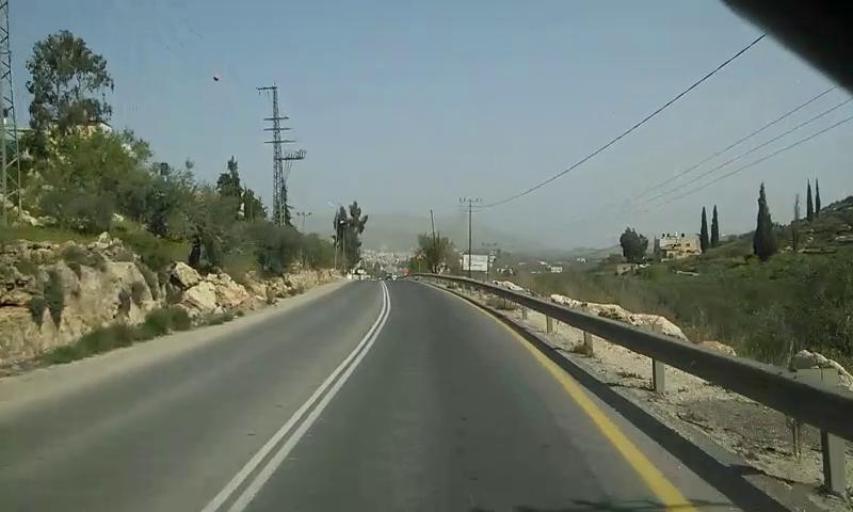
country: PS
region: West Bank
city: `Aynabus
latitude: 32.1313
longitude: 35.2577
